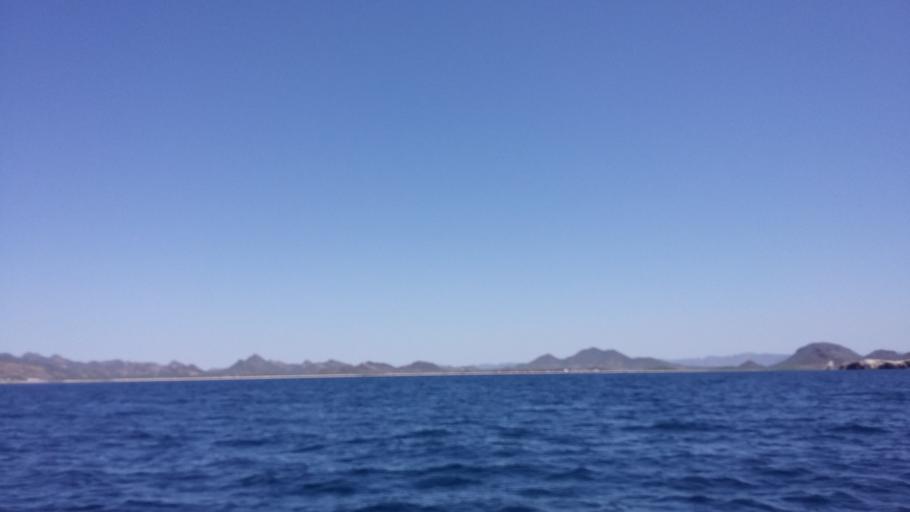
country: MX
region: Sonora
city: Heroica Guaymas
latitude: 27.9264
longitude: -111.0016
